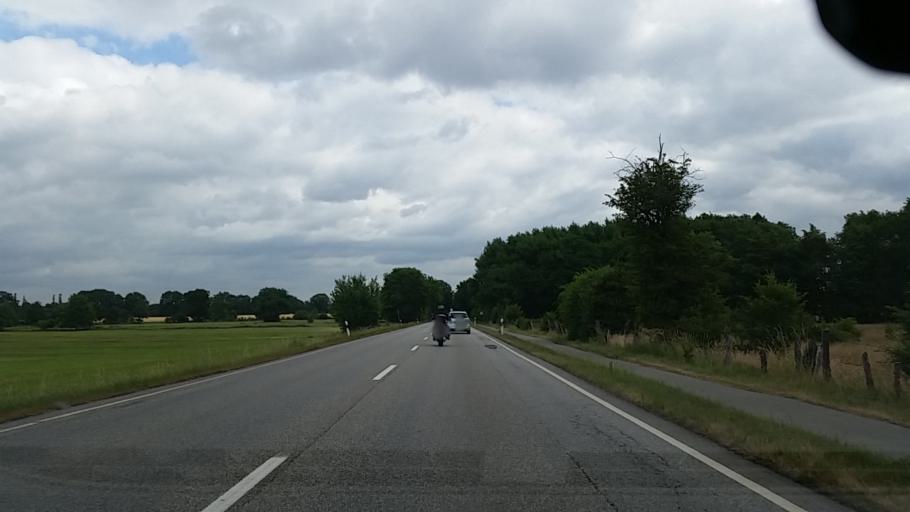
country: DE
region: Schleswig-Holstein
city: Tangstedt
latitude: 53.7170
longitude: 10.0821
